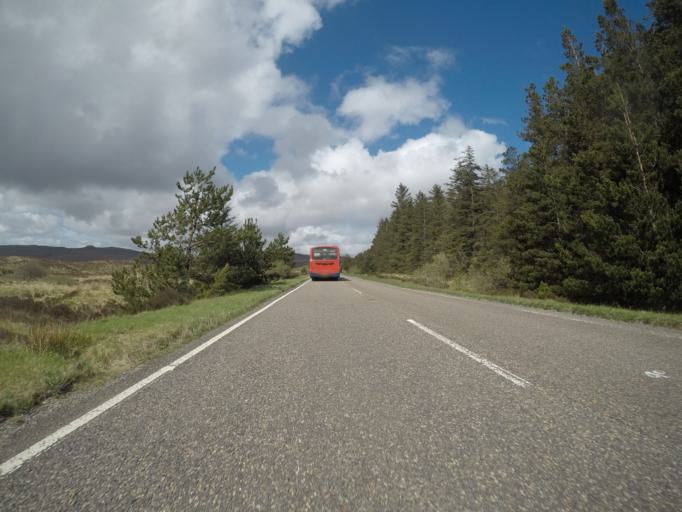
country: GB
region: Scotland
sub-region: Highland
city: Isle of Skye
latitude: 57.3122
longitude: -6.1965
